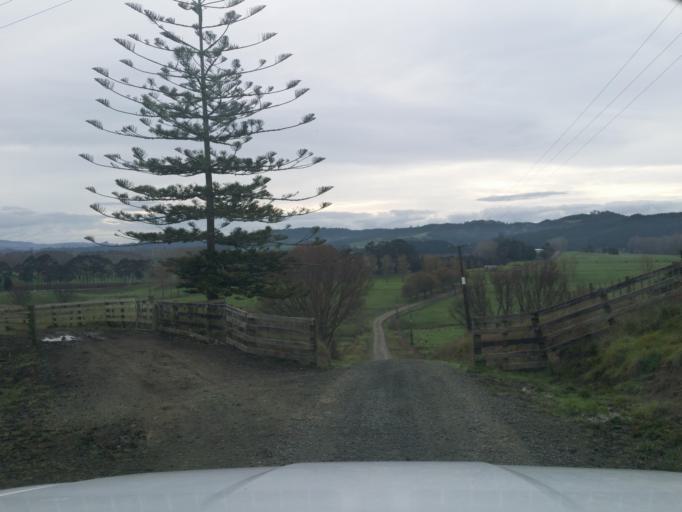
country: NZ
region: Northland
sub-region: Whangarei
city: Maungatapere
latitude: -35.8020
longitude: 174.0501
